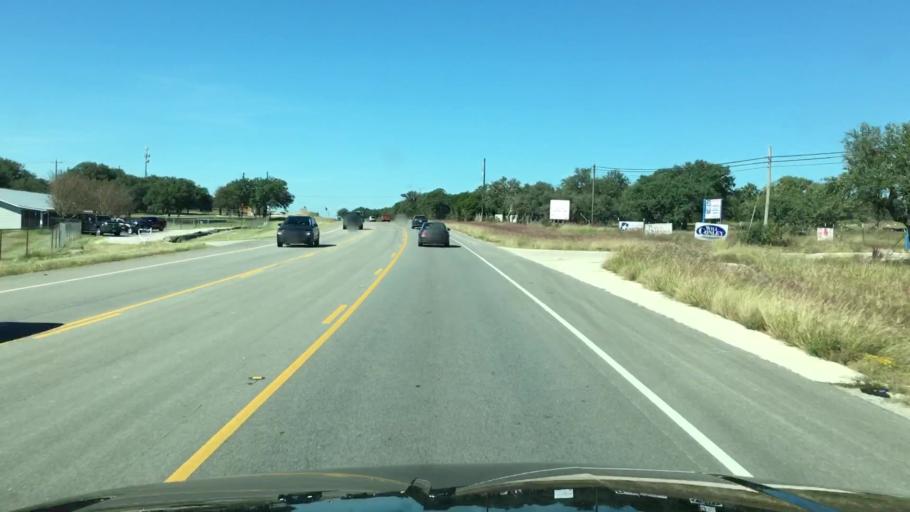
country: US
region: Texas
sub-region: Hays County
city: Dripping Springs
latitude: 30.1994
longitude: -98.1829
